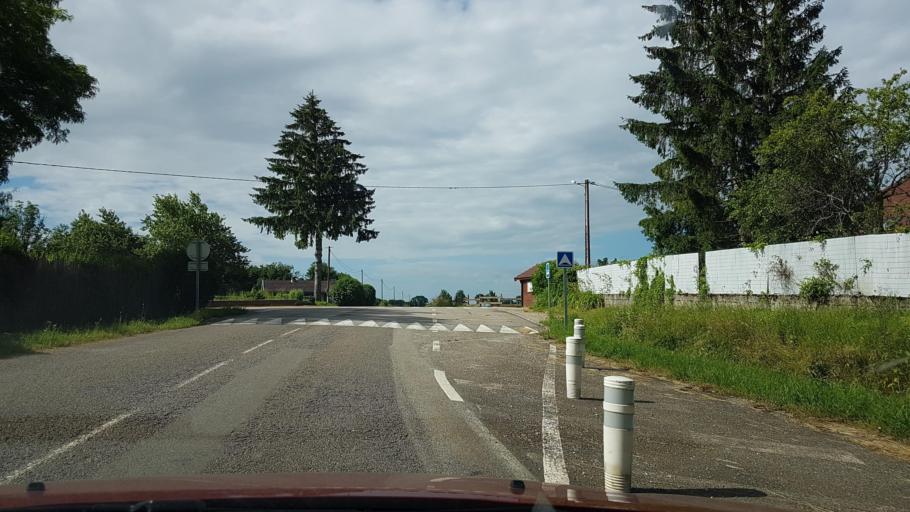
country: FR
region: Franche-Comte
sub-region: Departement du Jura
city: Clairvaux-les-Lacs
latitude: 46.5928
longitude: 5.7317
